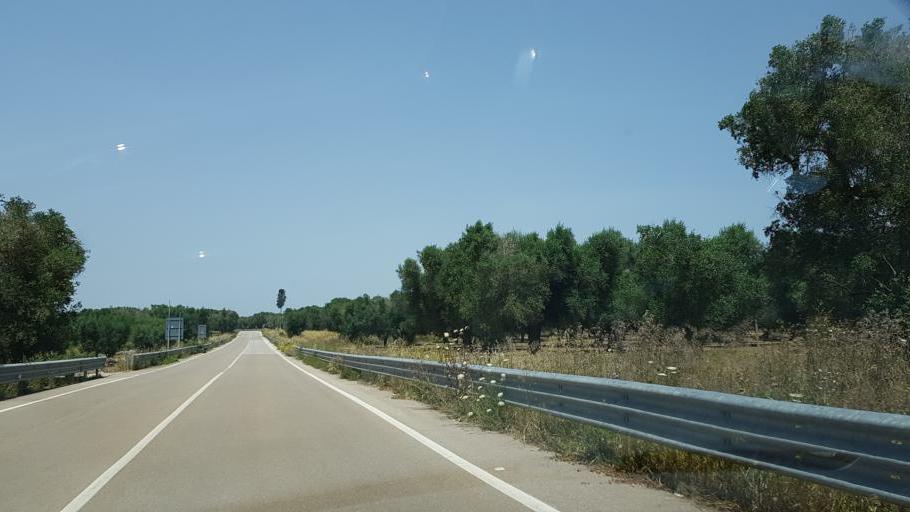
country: IT
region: Apulia
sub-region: Provincia di Brindisi
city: San Pancrazio Salentino
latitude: 40.4884
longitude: 17.8337
